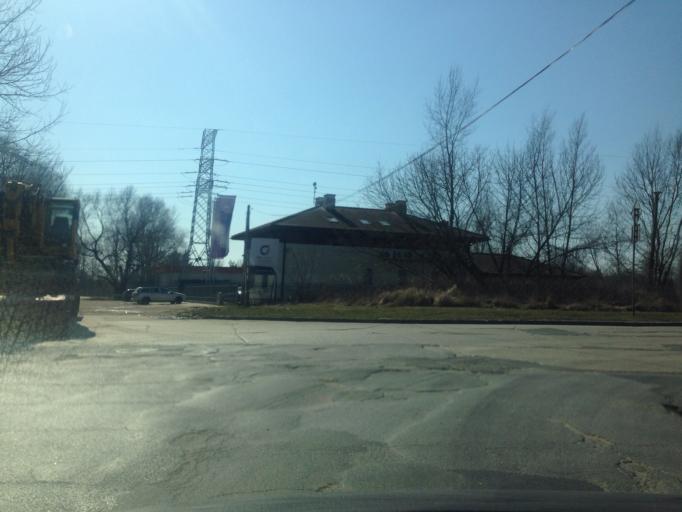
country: PL
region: Masovian Voivodeship
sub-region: Warszawa
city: Wilanow
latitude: 52.1815
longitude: 21.0898
